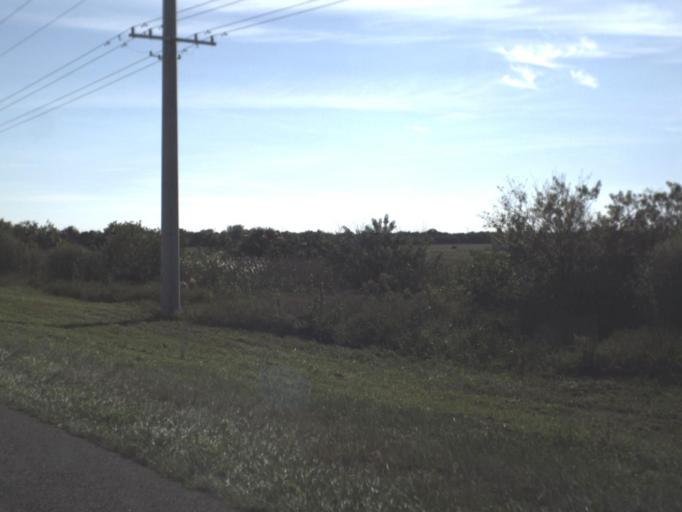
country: US
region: Florida
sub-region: Glades County
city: Moore Haven
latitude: 26.7789
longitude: -81.0830
